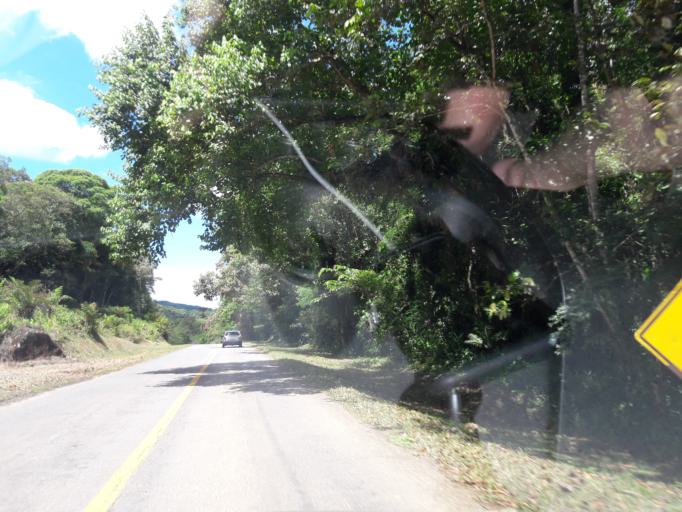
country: BR
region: Parana
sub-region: Antonina
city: Antonina
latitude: -25.4162
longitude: -48.8316
